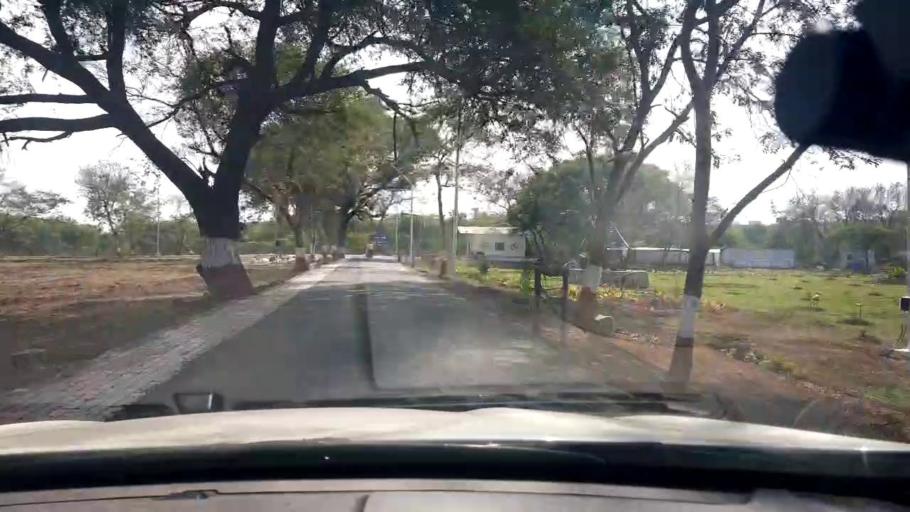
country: IN
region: Maharashtra
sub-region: Pune Division
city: Shivaji Nagar
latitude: 18.5406
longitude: 73.8558
